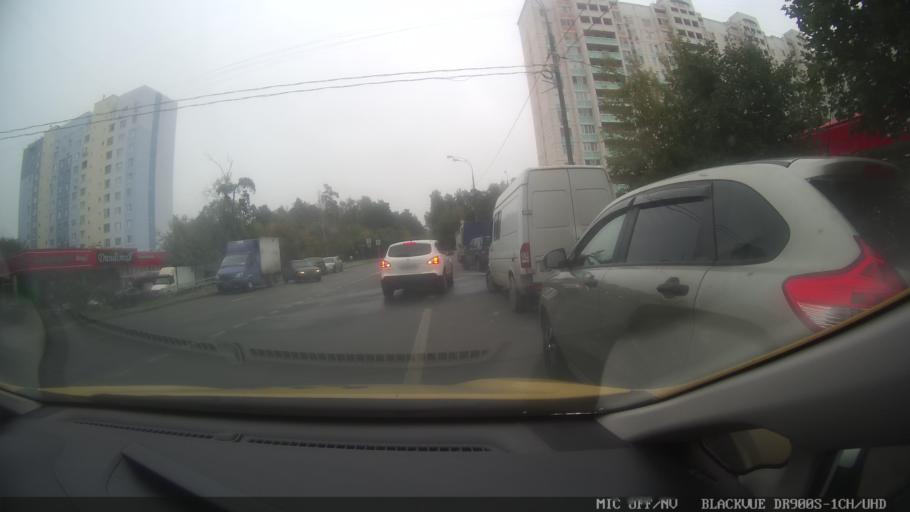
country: RU
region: Moscow
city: Nekrasovka
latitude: 55.6835
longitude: 37.9274
